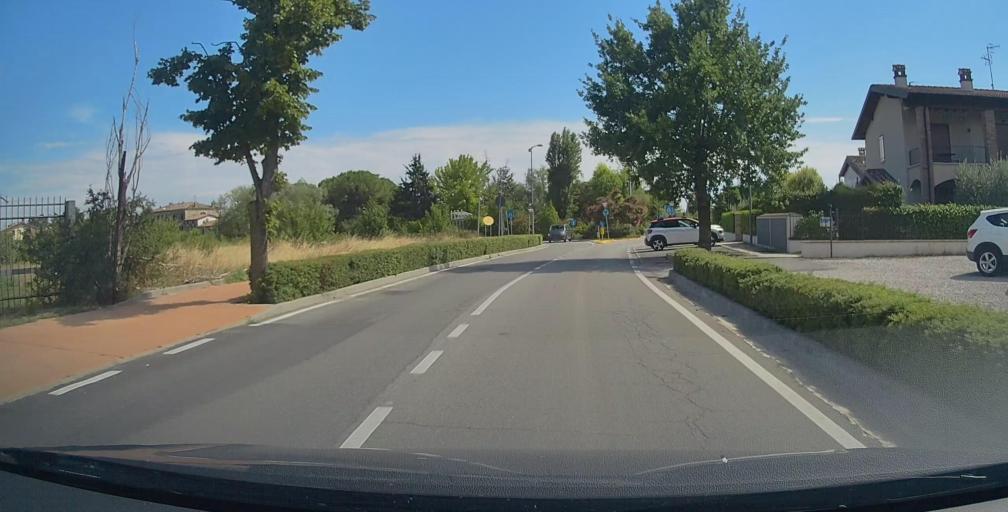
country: IT
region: Lombardy
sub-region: Provincia di Brescia
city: San Martino della Battaglia
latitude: 45.4504
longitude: 10.6172
